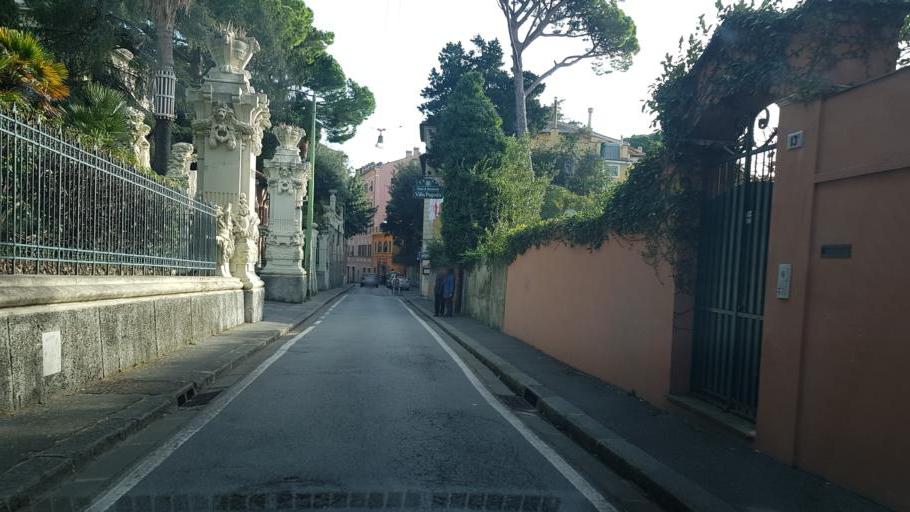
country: IT
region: Liguria
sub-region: Provincia di Genova
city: Bogliasco
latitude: 44.3812
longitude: 9.0490
